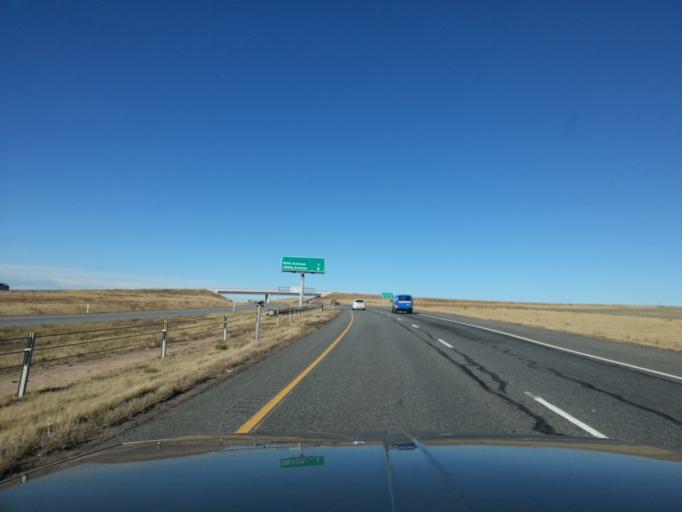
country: US
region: Colorado
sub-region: Adams County
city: Aurora
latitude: 39.8527
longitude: -104.7467
